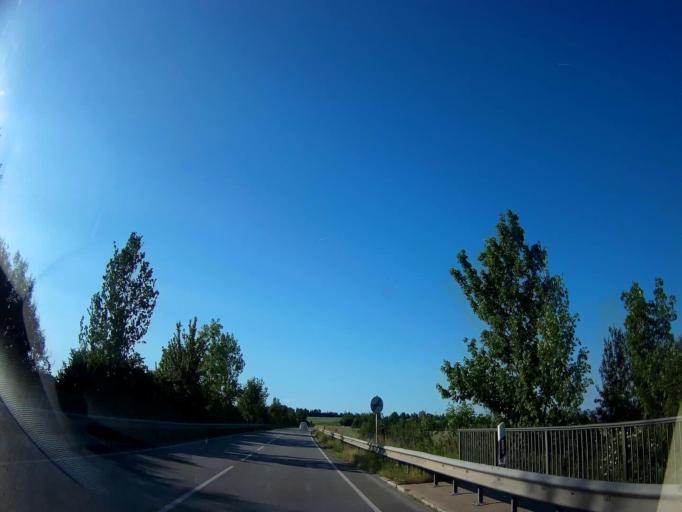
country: DE
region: Bavaria
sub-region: Lower Bavaria
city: Pilsting
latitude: 48.7332
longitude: 12.6589
